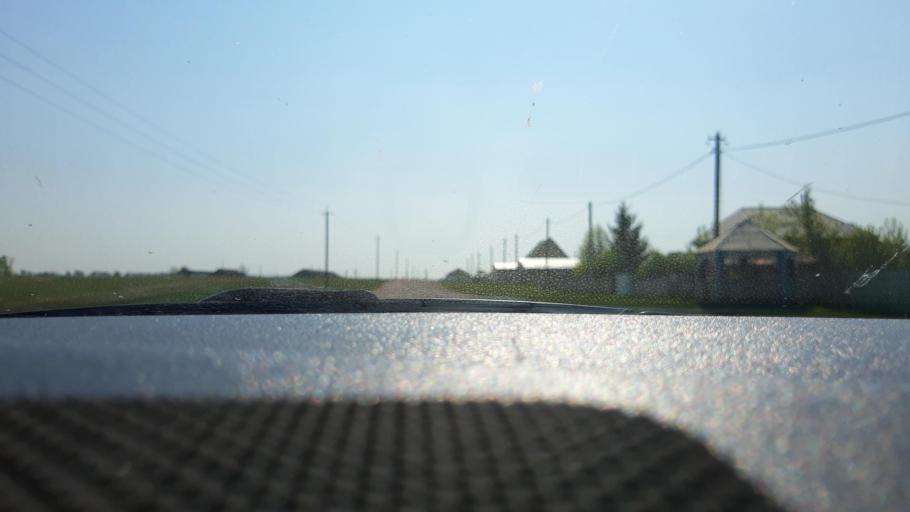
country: RU
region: Bashkortostan
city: Chishmy
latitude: 54.4504
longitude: 55.3219
